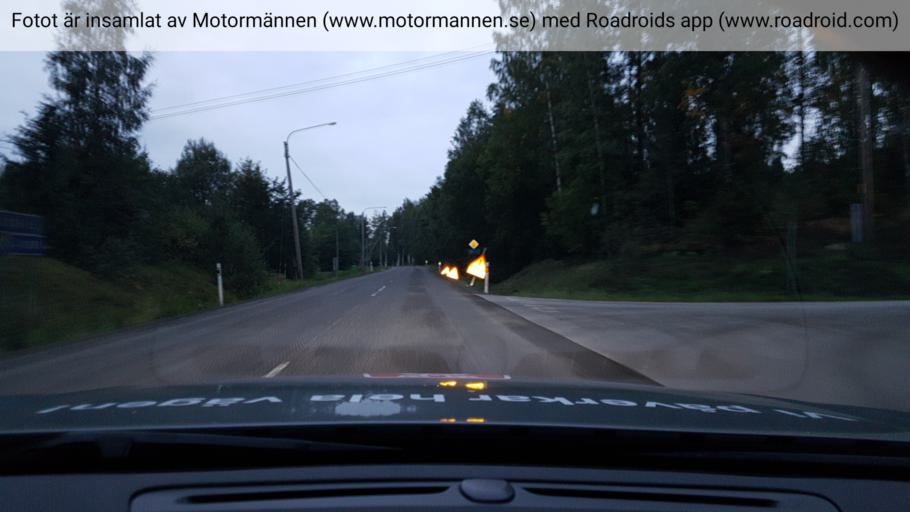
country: SE
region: OErebro
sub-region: Nora Kommun
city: As
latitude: 59.4630
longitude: 14.8577
